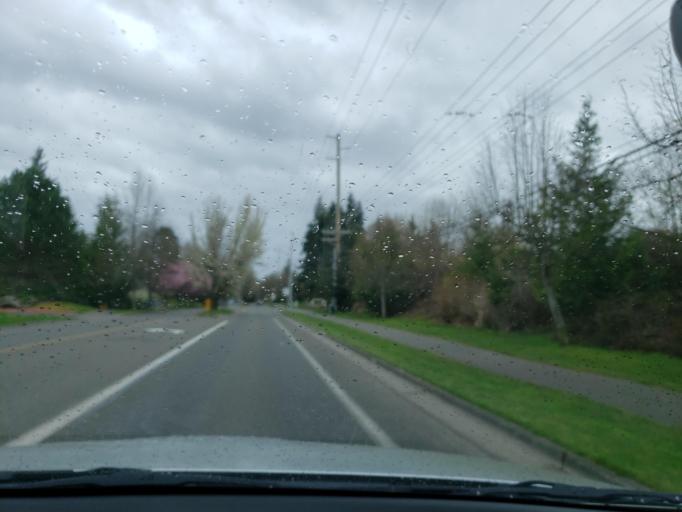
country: US
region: Washington
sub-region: Snohomish County
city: Meadowdale
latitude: 47.8900
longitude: -122.3117
